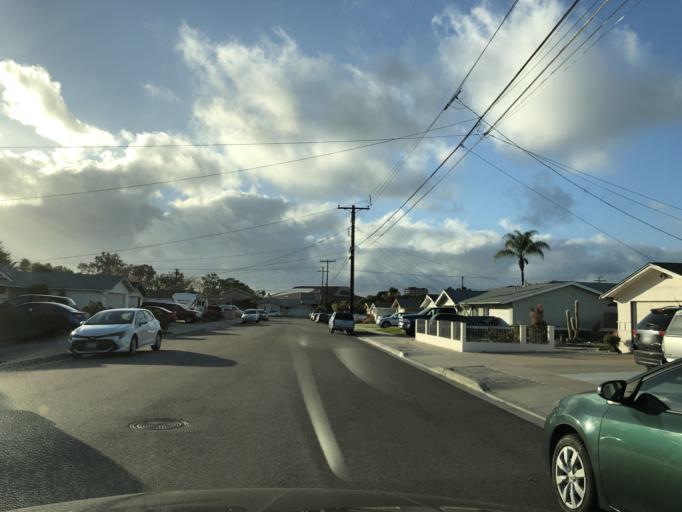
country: US
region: California
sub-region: San Diego County
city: San Diego
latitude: 32.8178
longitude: -117.1739
